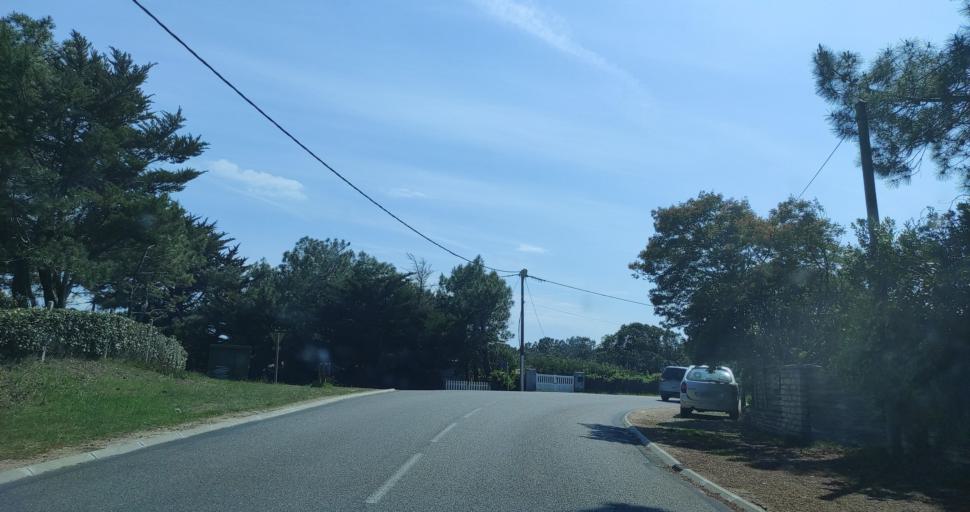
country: FR
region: Aquitaine
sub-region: Departement de la Gironde
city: Arcachon
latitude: 44.6477
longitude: -1.2536
